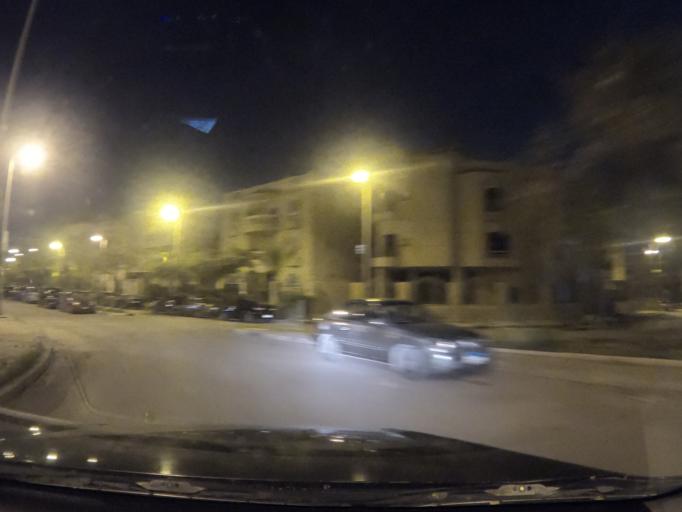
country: EG
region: Muhafazat al Qahirah
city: Cairo
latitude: 30.0152
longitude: 31.4264
